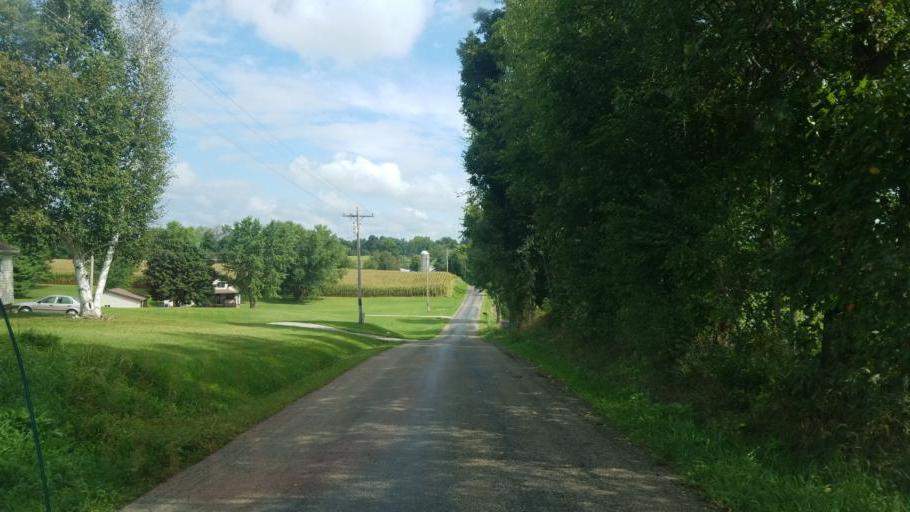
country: US
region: Ohio
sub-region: Knox County
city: Mount Vernon
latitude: 40.4607
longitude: -82.4669
